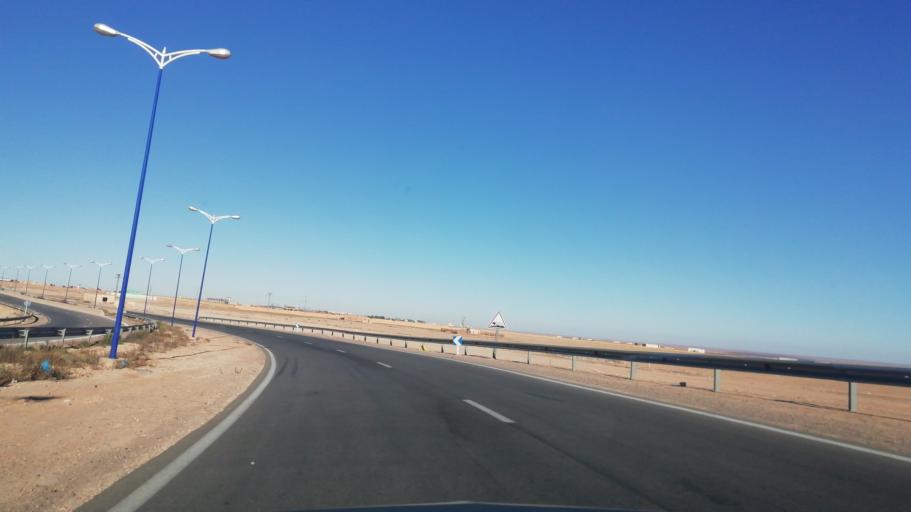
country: DZ
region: Wilaya de Naama
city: Naama
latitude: 33.5136
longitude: -0.2780
